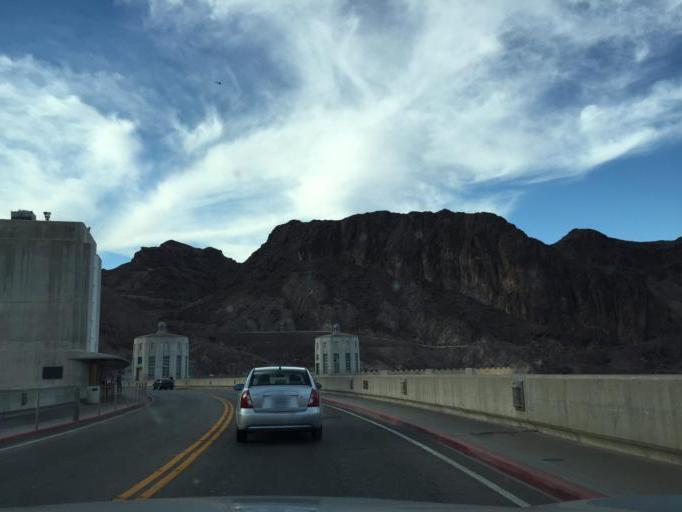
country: US
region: Nevada
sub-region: Clark County
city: Boulder City
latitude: 36.0156
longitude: -114.7369
